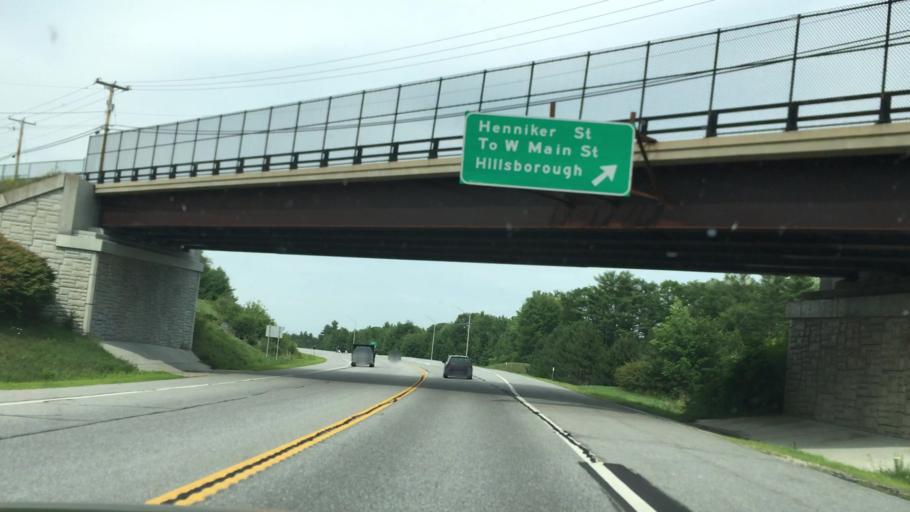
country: US
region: New Hampshire
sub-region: Hillsborough County
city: Hillsboro
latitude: 43.1301
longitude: -71.8854
